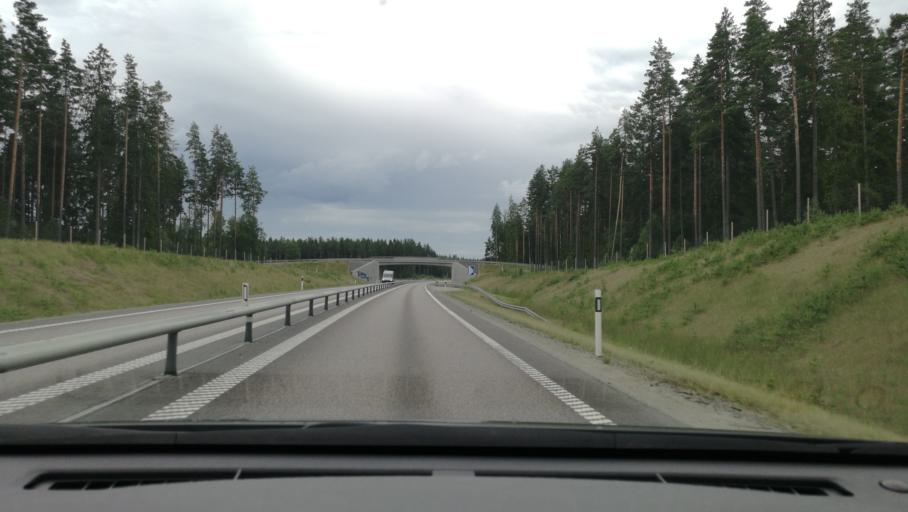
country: SE
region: Soedermanland
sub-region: Katrineholms Kommun
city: Katrineholm
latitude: 58.9875
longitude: 16.2648
